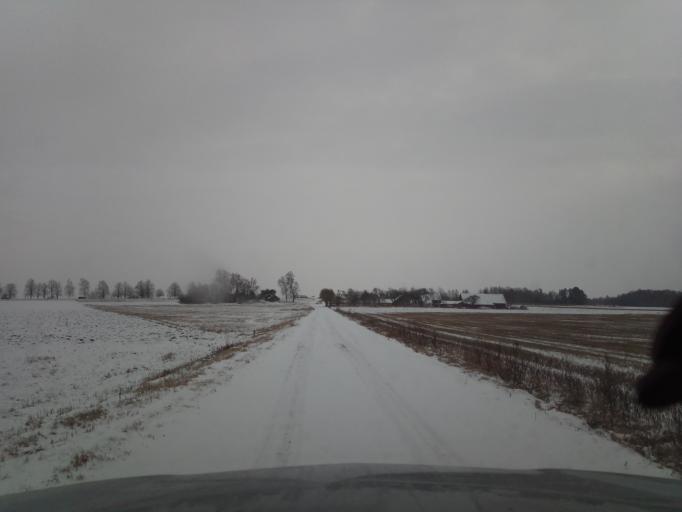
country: LT
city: Ramygala
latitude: 55.6040
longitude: 24.3415
